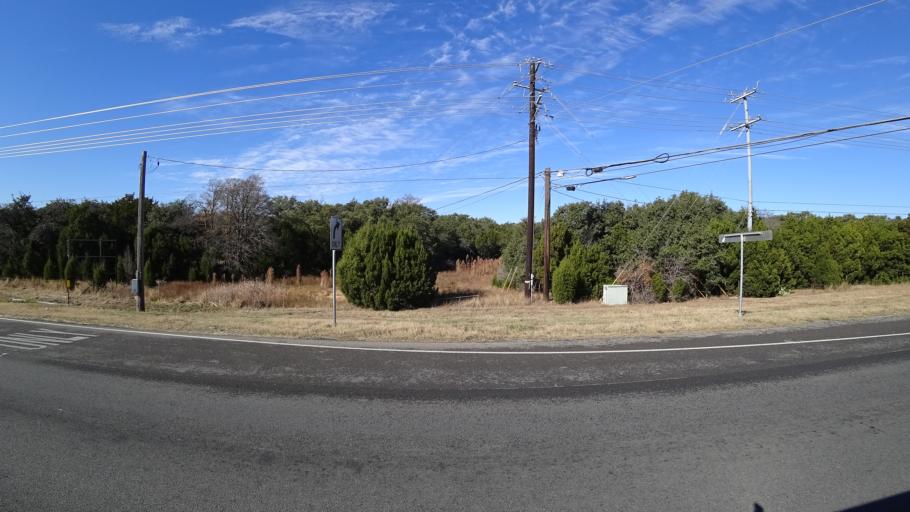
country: US
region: Texas
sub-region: Williamson County
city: Brushy Creek
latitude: 30.5089
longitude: -97.7753
